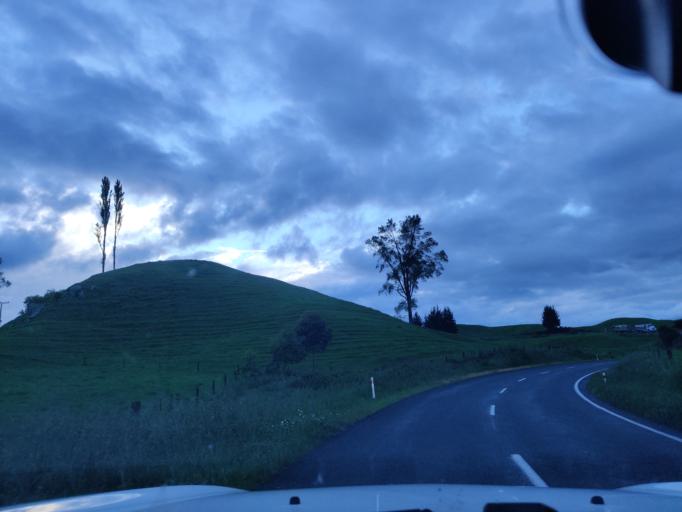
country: NZ
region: Waikato
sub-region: South Waikato District
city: Tokoroa
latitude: -38.2020
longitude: 175.8122
